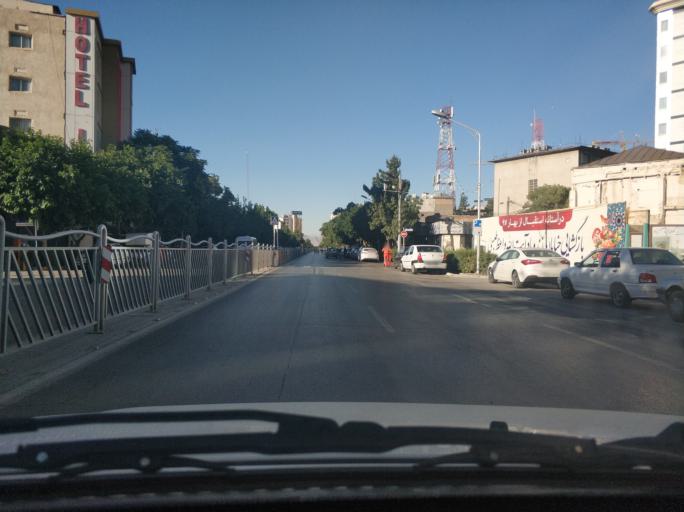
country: IR
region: Razavi Khorasan
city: Mashhad
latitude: 36.2918
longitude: 59.6074
